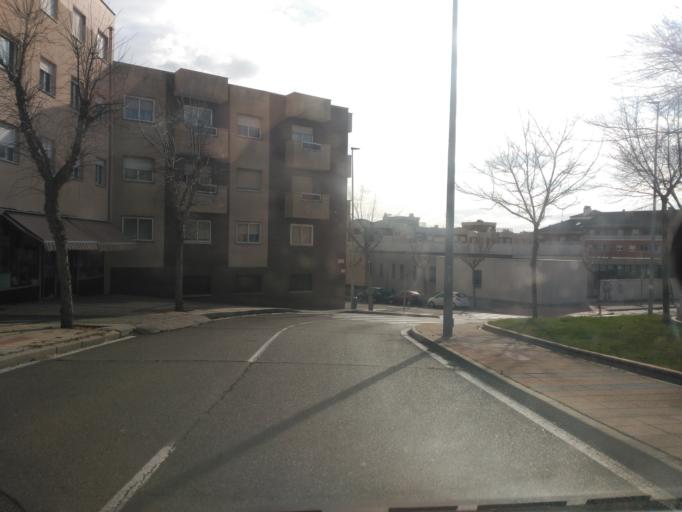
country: ES
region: Castille and Leon
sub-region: Provincia de Salamanca
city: Salamanca
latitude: 40.9640
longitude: -5.6483
